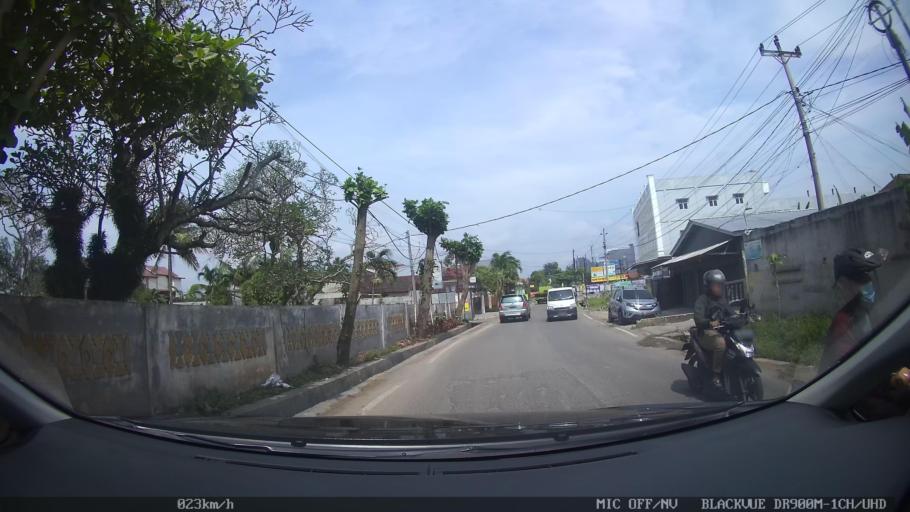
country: ID
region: Lampung
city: Kedaton
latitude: -5.3916
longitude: 105.2852
